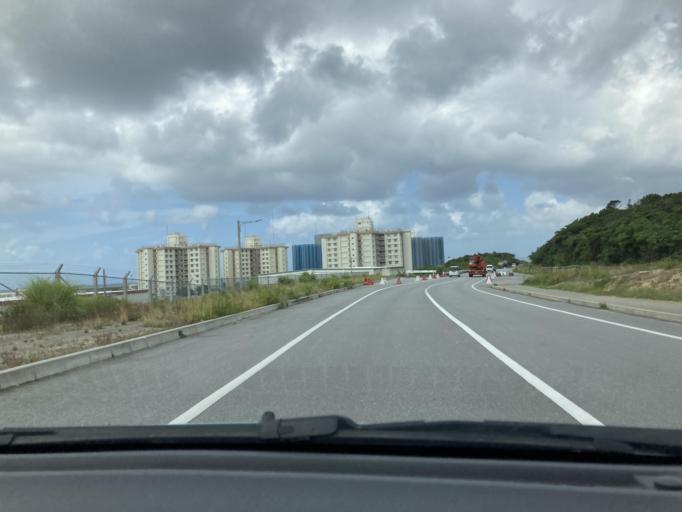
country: JP
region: Okinawa
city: Ginowan
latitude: 26.2637
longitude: 127.7086
